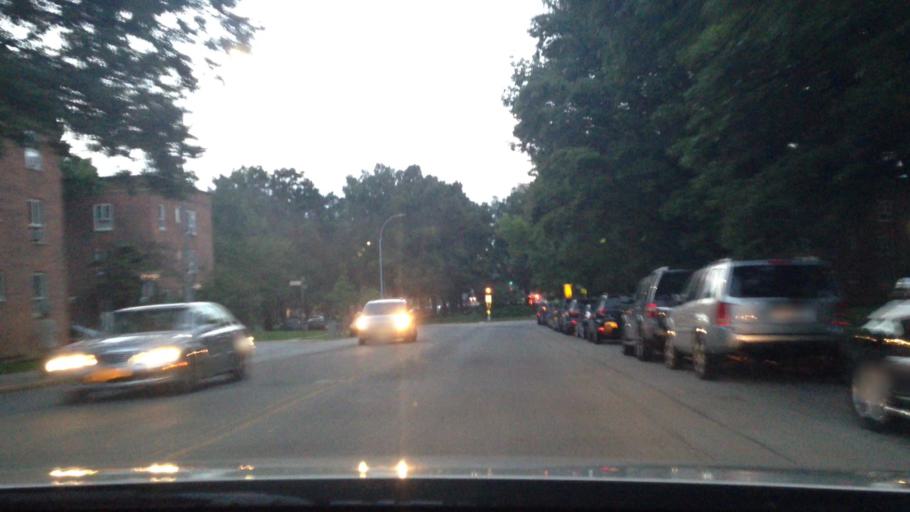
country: US
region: New York
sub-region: Queens County
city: Jamaica
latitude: 40.7340
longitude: -73.7834
